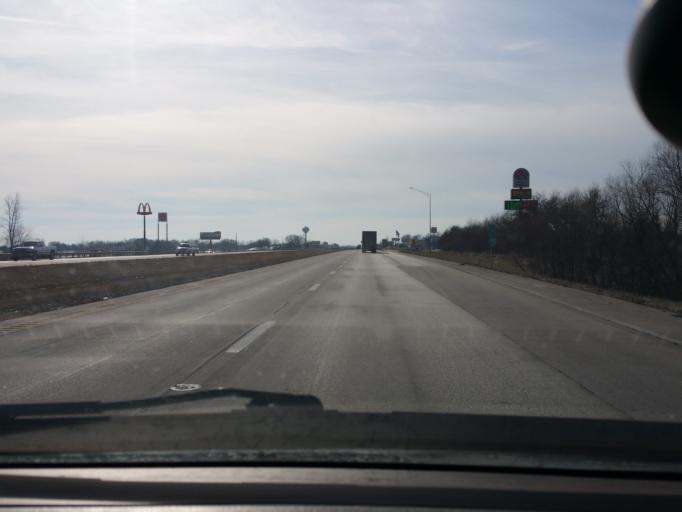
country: US
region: Missouri
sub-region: Clay County
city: Kearney
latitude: 39.3717
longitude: -94.3704
